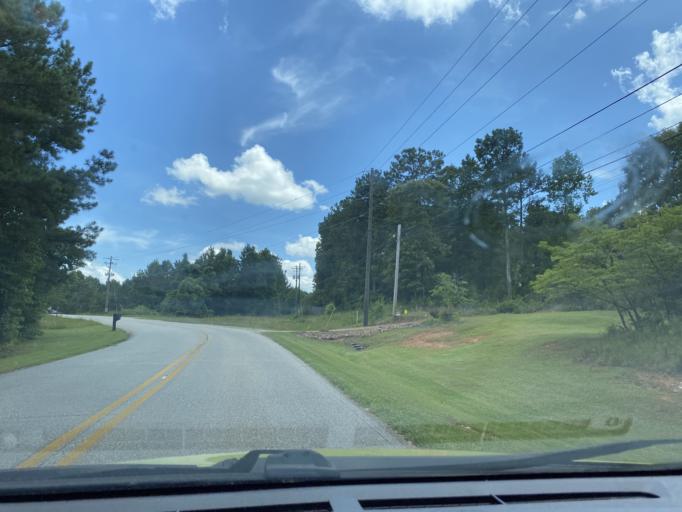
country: US
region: Georgia
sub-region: Fayette County
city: Peachtree City
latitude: 33.4103
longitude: -84.6922
